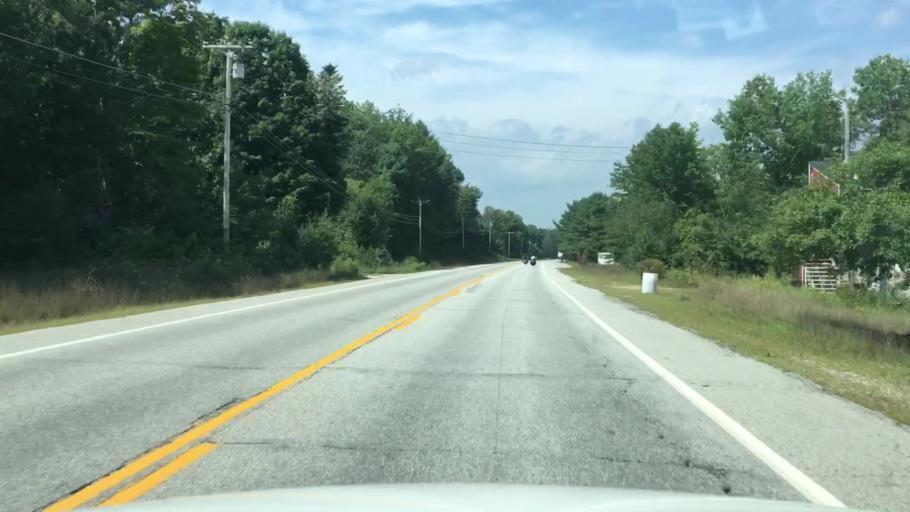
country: US
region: Maine
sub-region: Oxford County
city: Peru
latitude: 44.4970
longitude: -70.3924
